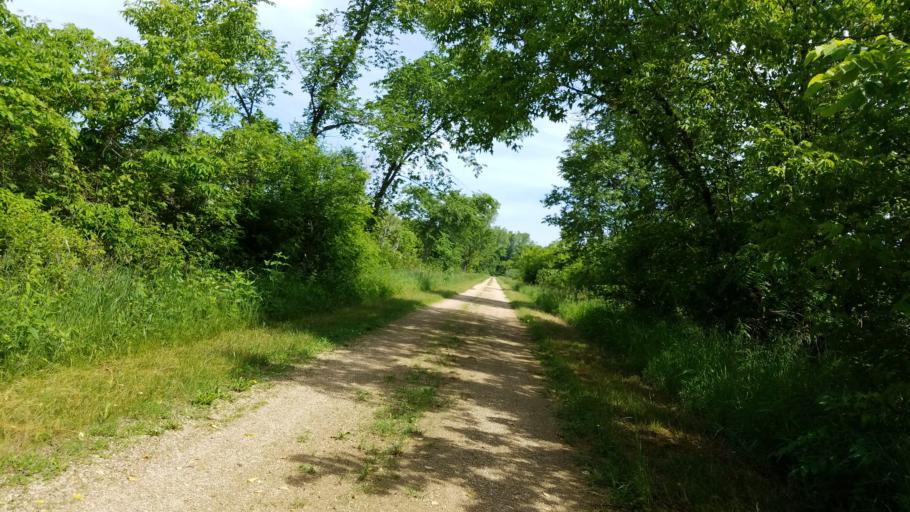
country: US
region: Wisconsin
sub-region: Dunn County
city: Menomonie
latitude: 44.7914
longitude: -91.9467
